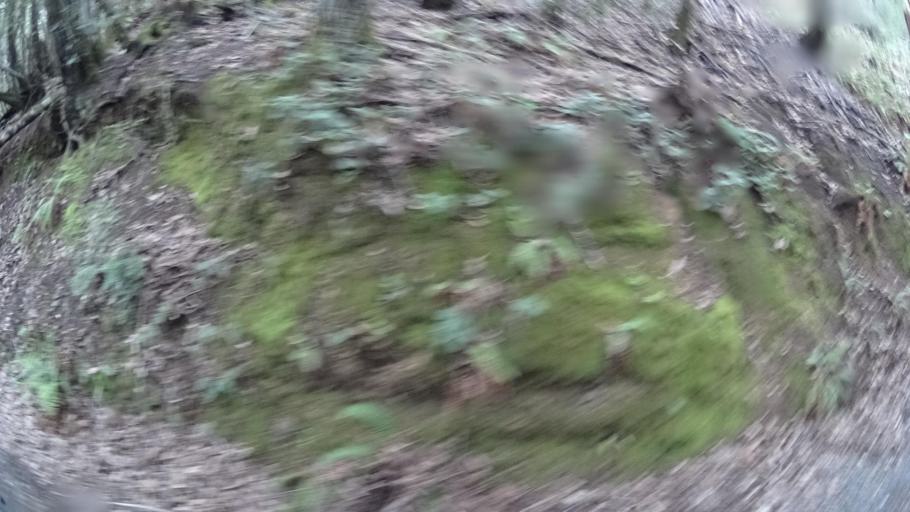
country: US
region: California
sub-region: Humboldt County
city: Blue Lake
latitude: 40.8696
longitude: -123.9005
